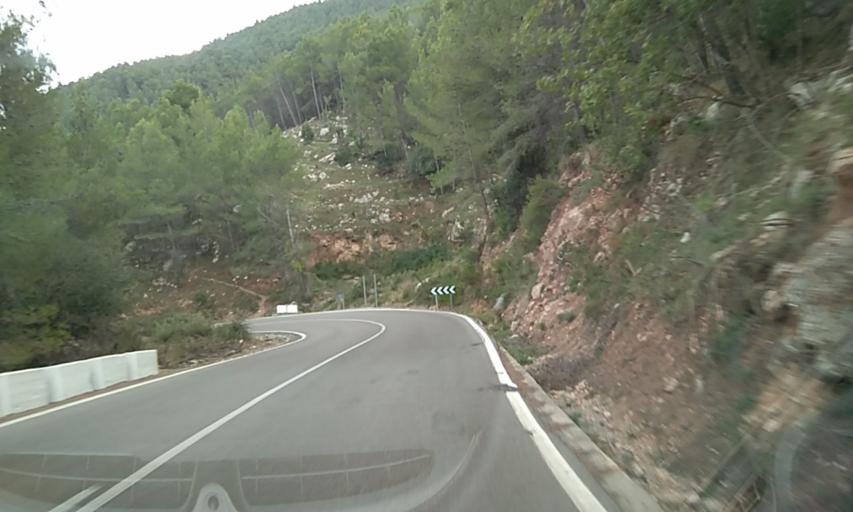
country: ES
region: Valencia
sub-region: Provincia de Castello
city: Montanejos
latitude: 40.0833
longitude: -0.5483
